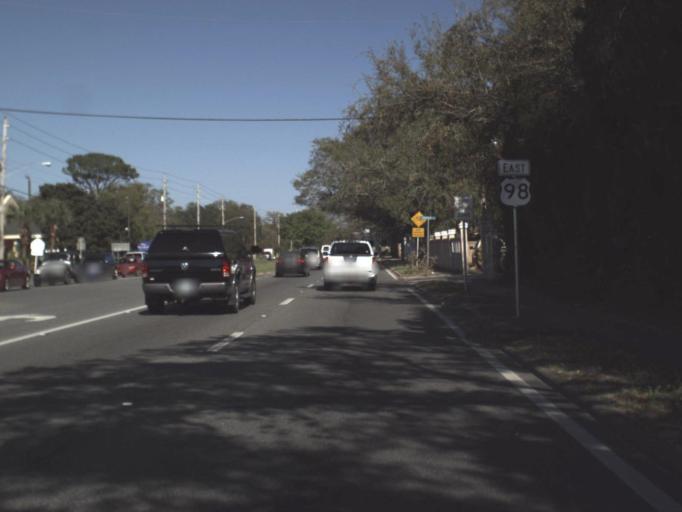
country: US
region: Florida
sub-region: Okaloosa County
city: Mary Esther
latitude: 30.4093
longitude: -86.6549
